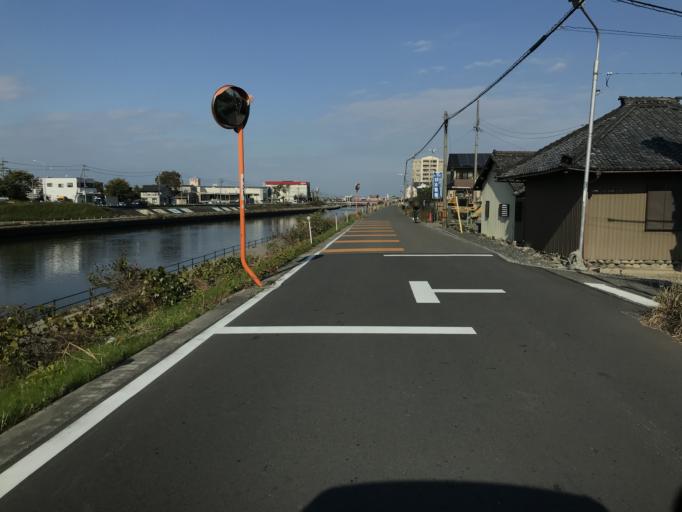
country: JP
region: Aichi
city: Nagoya-shi
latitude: 35.1851
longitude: 136.8462
